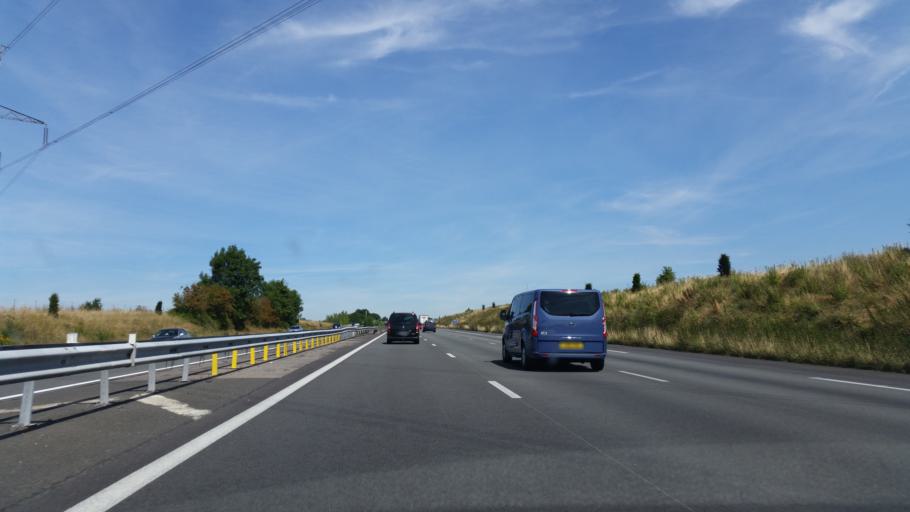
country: FR
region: Picardie
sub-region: Departement de la Somme
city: Peronne
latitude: 49.9734
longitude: 2.8638
